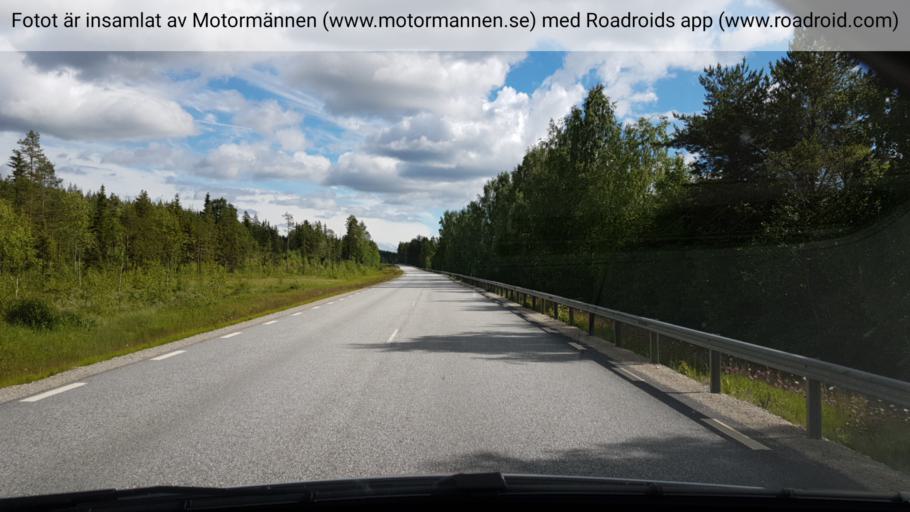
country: SE
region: Vaesterbotten
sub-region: Vindelns Kommun
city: Vindeln
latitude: 64.1893
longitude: 19.4641
